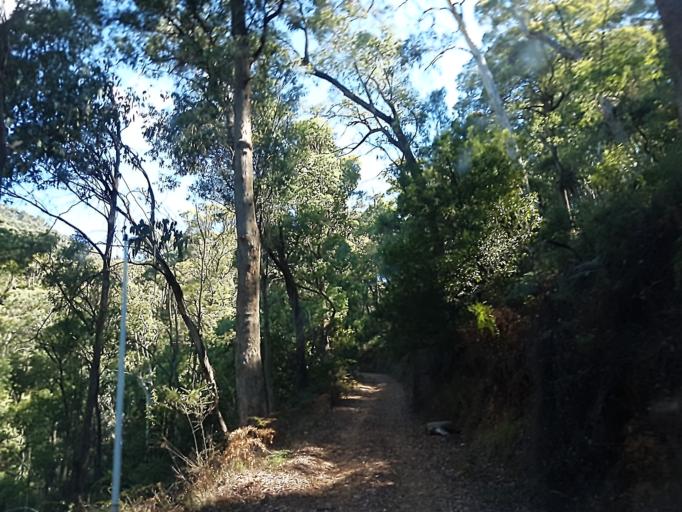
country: AU
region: Victoria
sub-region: Alpine
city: Mount Beauty
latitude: -36.8822
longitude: 147.0385
